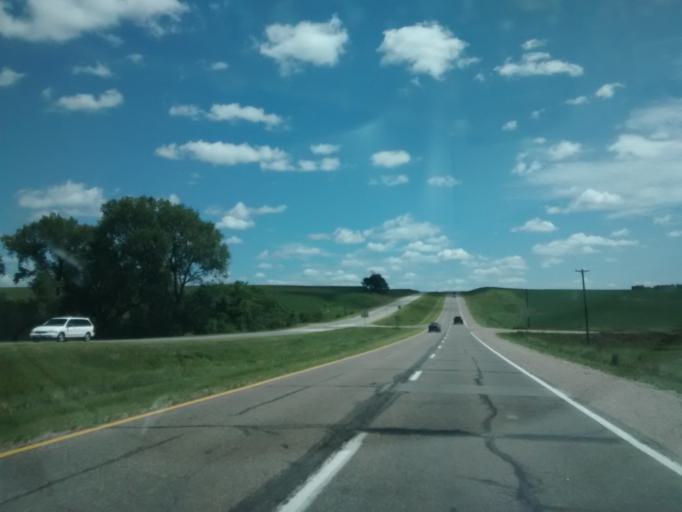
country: US
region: Iowa
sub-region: Woodbury County
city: Moville
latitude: 42.4749
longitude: -96.1564
